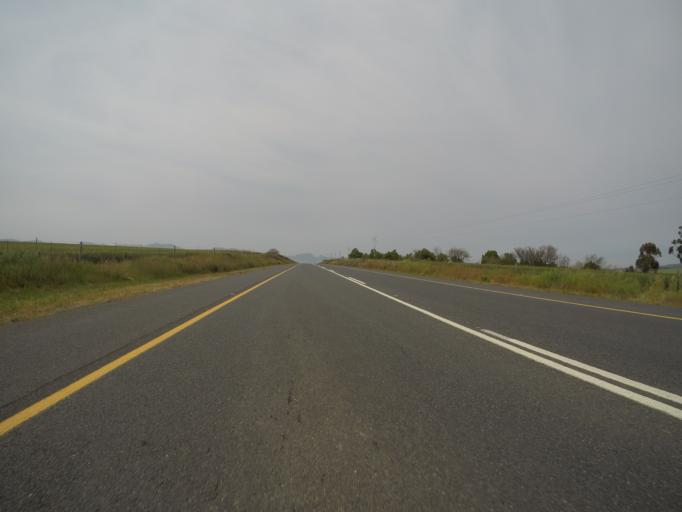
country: ZA
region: Western Cape
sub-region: Cape Winelands District Municipality
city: Noorder-Paarl
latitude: -33.5580
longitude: 18.8764
